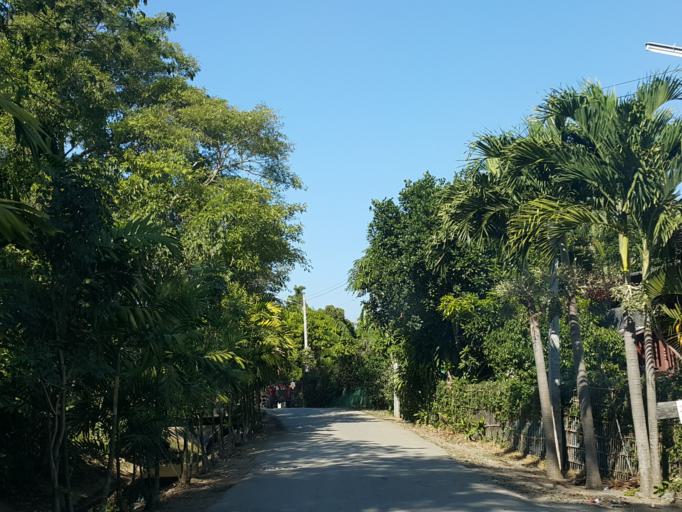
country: TH
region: Chiang Mai
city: San Sai
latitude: 18.8832
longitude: 98.9828
